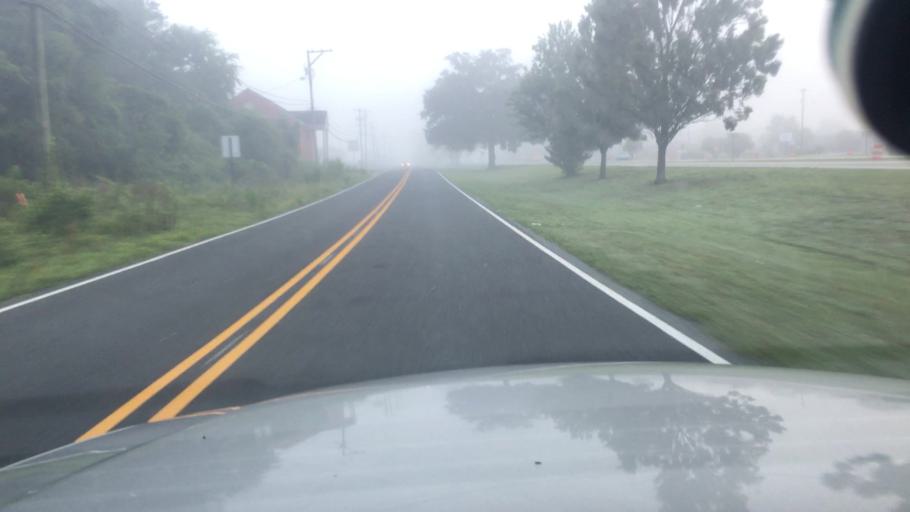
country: US
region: North Carolina
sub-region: Cumberland County
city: Fayetteville
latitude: 35.0099
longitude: -78.8978
